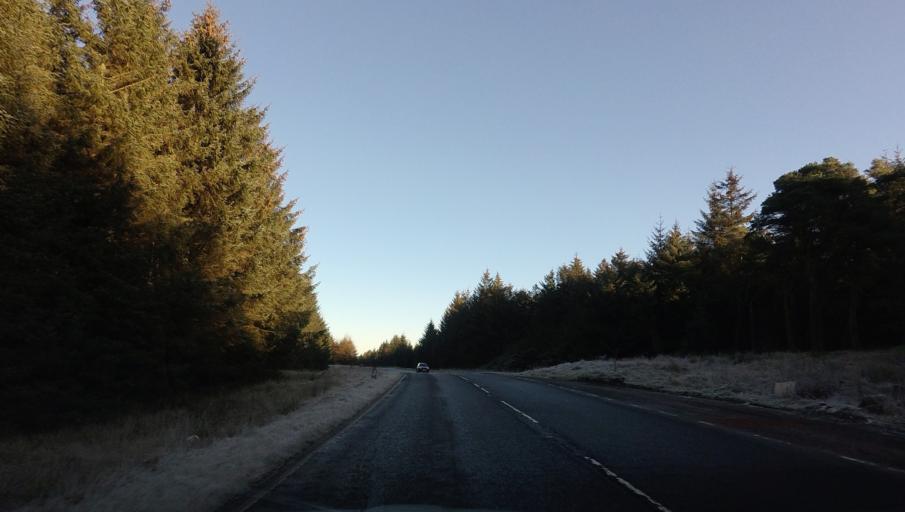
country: GB
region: Scotland
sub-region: West Lothian
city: Fauldhouse
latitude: 55.8134
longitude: -3.7053
